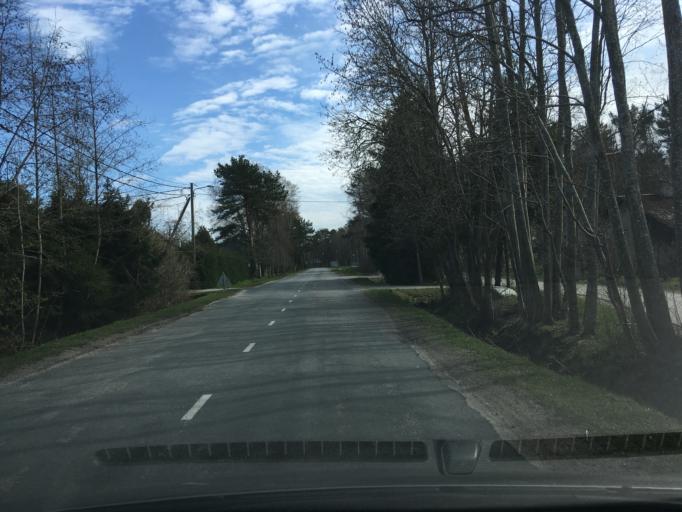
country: EE
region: Harju
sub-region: Joelaehtme vald
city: Loo
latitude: 59.4804
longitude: 24.9444
